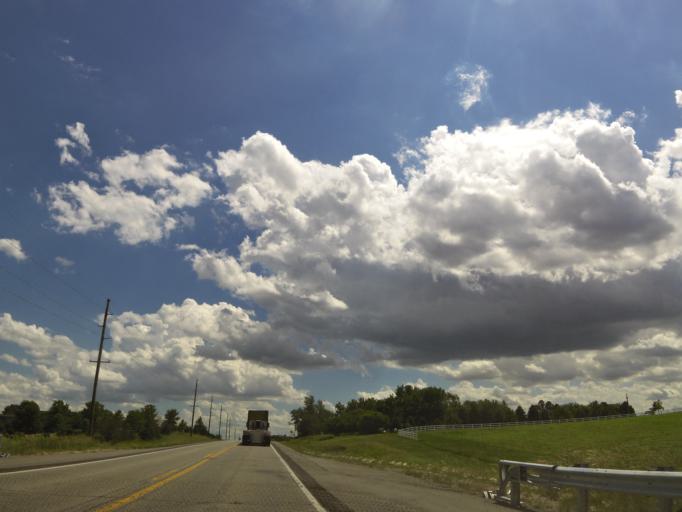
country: US
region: Iowa
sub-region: Benton County
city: Urbana
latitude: 42.2653
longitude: -91.8905
